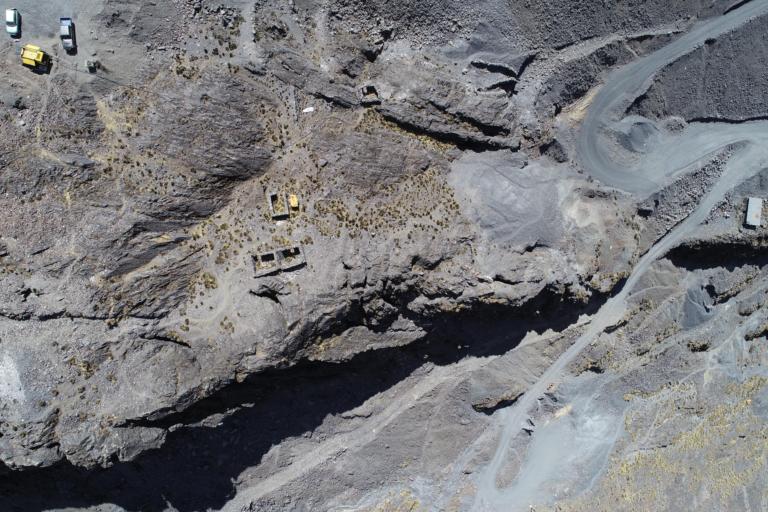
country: BO
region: La Paz
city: Sorata
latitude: -15.6696
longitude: -68.5630
